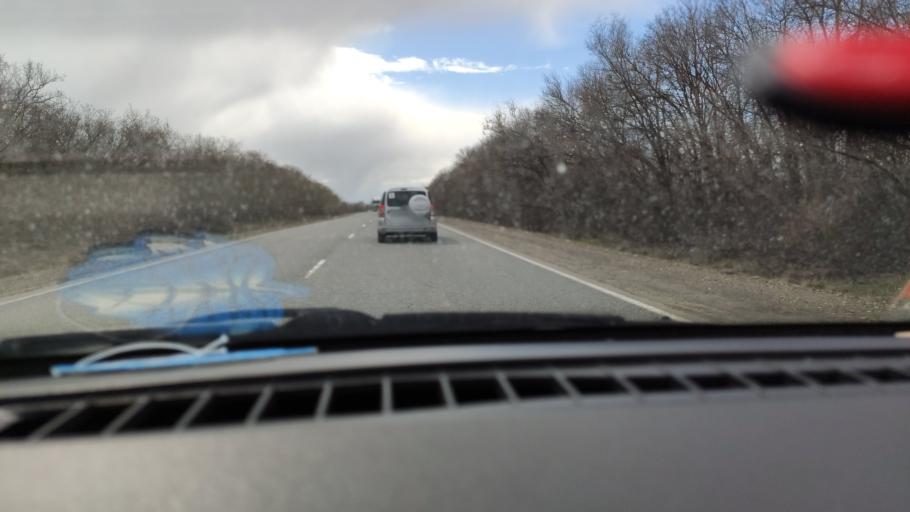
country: RU
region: Samara
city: Zhigulevsk
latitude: 53.2894
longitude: 49.3277
